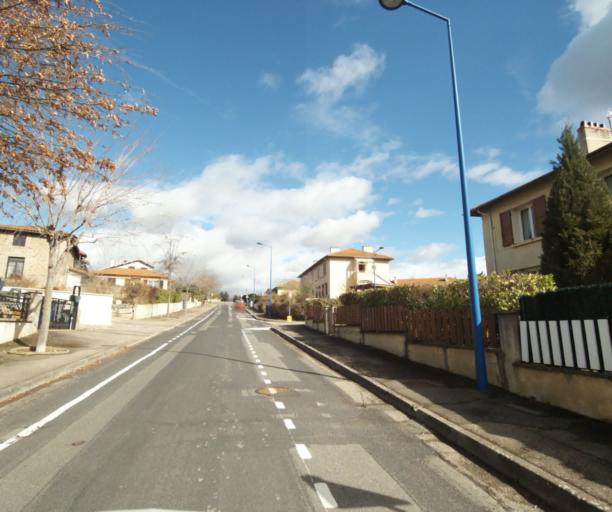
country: FR
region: Rhone-Alpes
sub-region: Departement de la Loire
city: La Talaudiere
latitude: 45.4836
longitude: 4.4316
